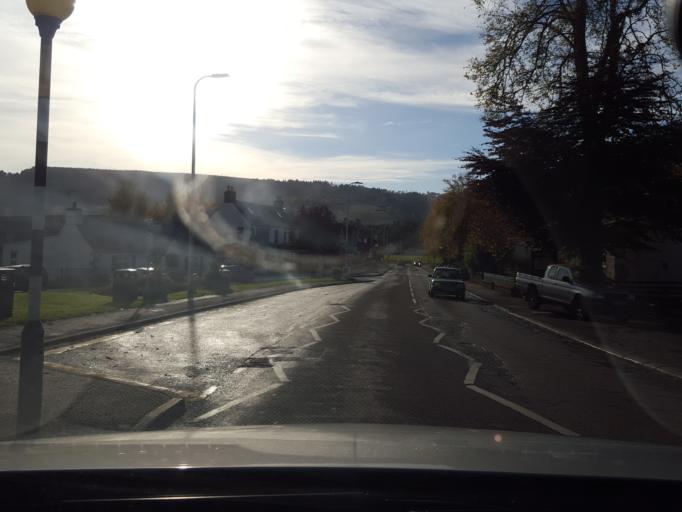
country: GB
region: Scotland
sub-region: Highland
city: Beauly
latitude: 57.3362
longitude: -4.4802
